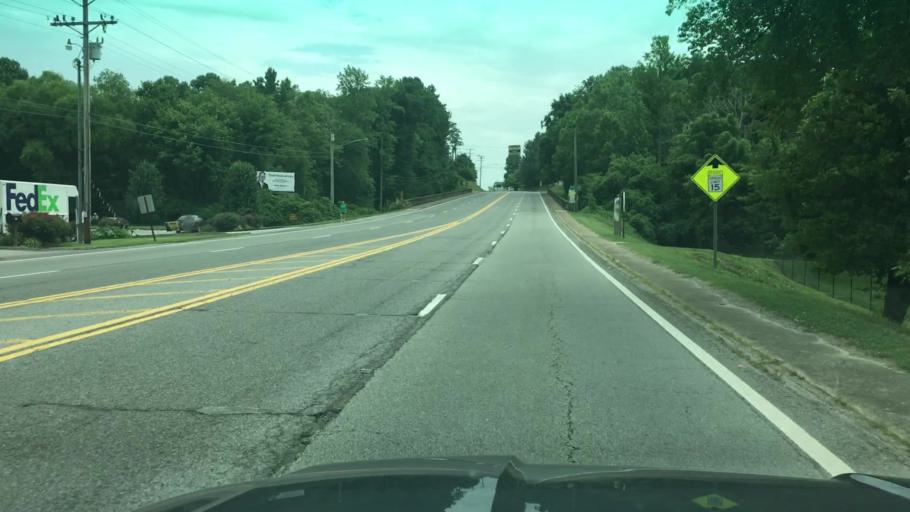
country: US
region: Tennessee
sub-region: Coffee County
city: Manchester
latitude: 35.4814
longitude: -86.0790
